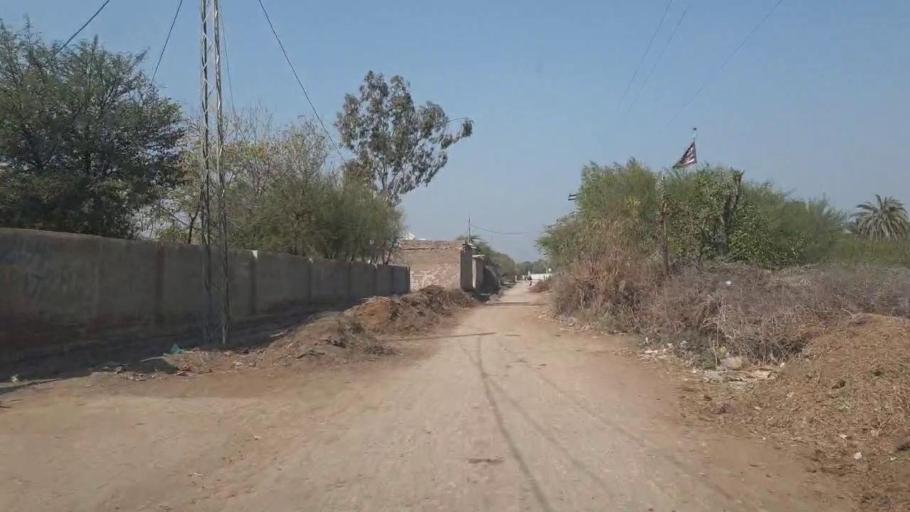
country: PK
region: Sindh
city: Tando Allahyar
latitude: 25.4304
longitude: 68.8382
